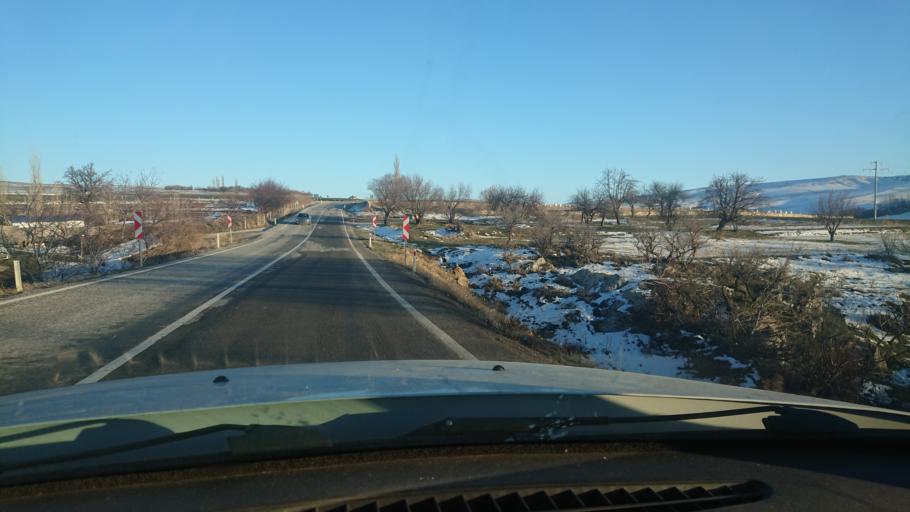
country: TR
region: Aksaray
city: Ortakoy
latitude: 38.7539
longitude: 33.9343
